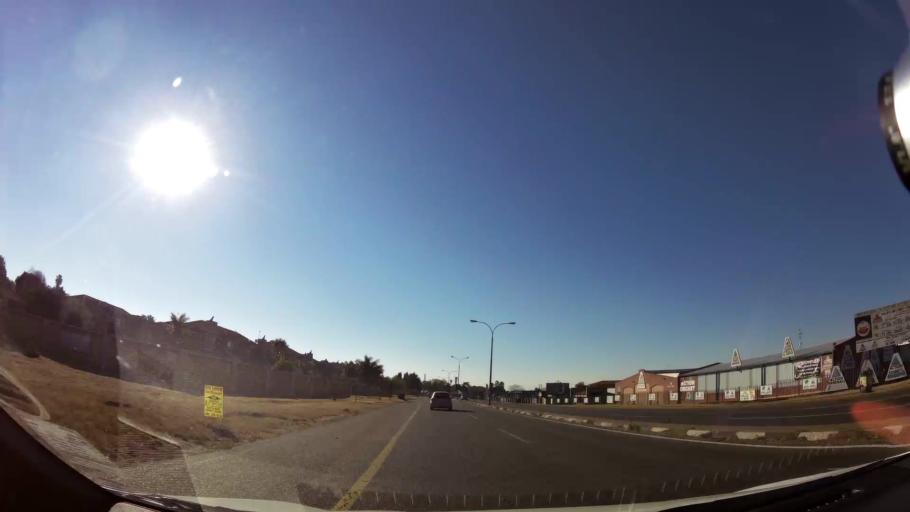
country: ZA
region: Gauteng
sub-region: Ekurhuleni Metropolitan Municipality
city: Germiston
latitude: -26.2868
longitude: 28.1027
